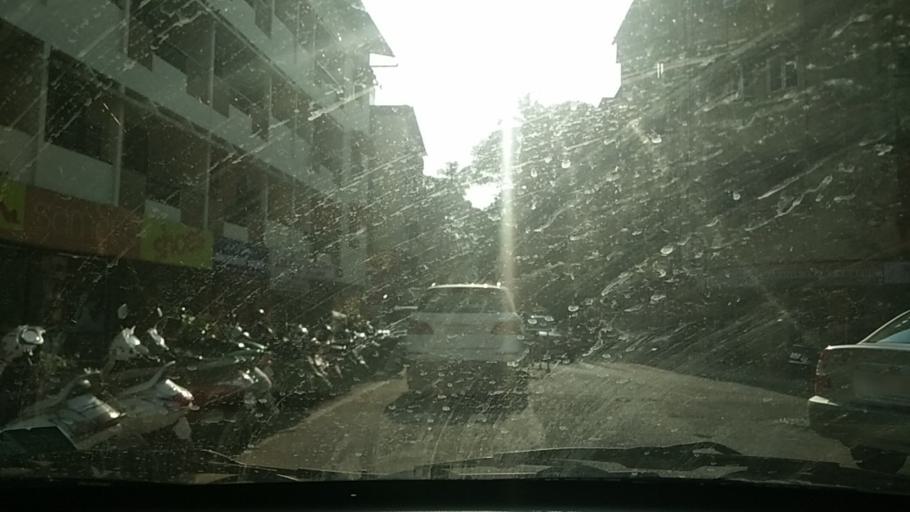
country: IN
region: Goa
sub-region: North Goa
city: Panaji
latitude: 15.4972
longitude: 73.8277
